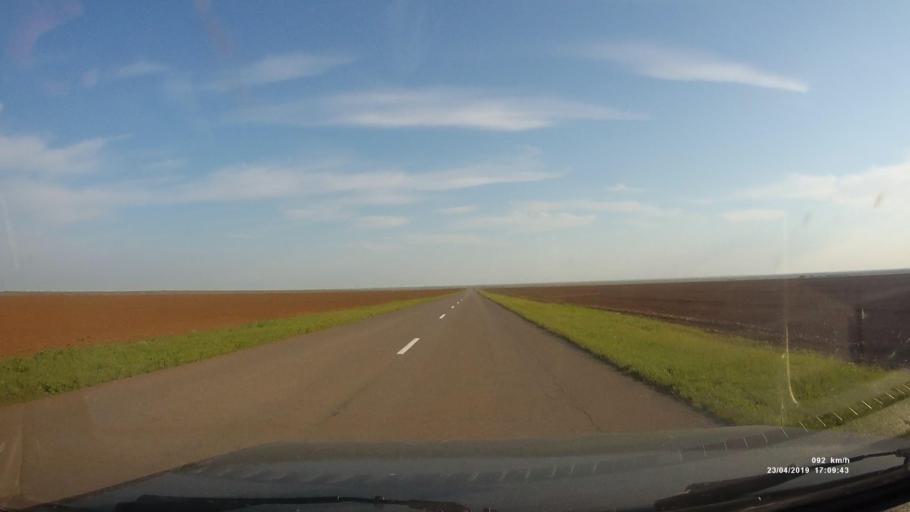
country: RU
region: Kalmykiya
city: Priyutnoye
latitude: 46.2547
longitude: 43.4842
